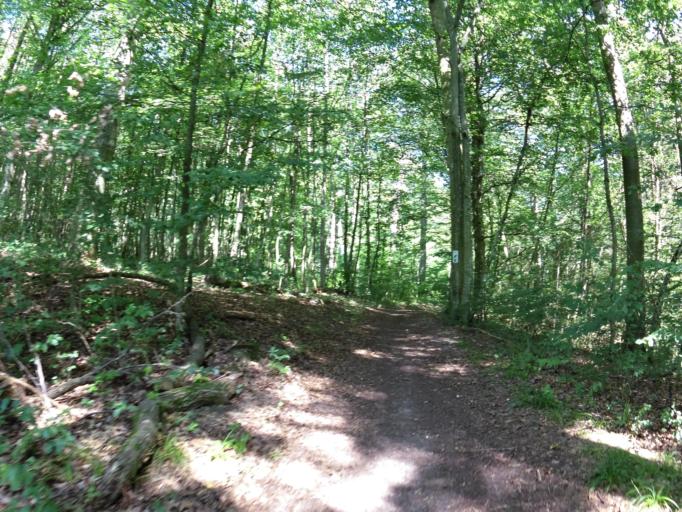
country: DE
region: Bavaria
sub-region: Regierungsbezirk Unterfranken
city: Gadheim
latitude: 49.8450
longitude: 9.8941
